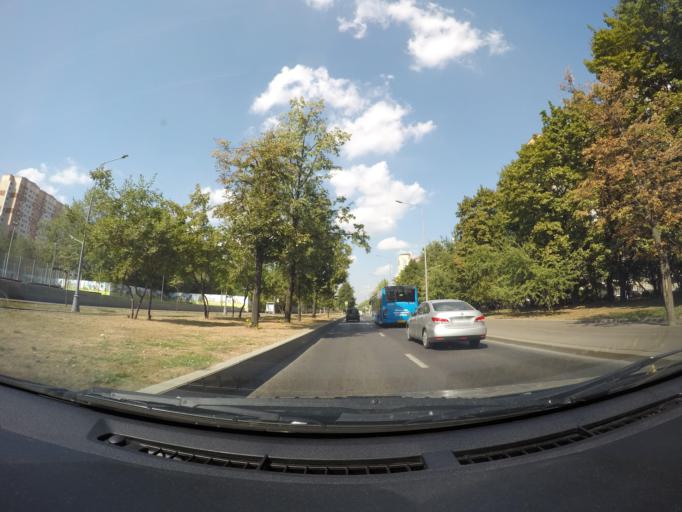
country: RU
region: Moskovskaya
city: Levoberezhnaya
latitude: 55.8702
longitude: 37.4837
